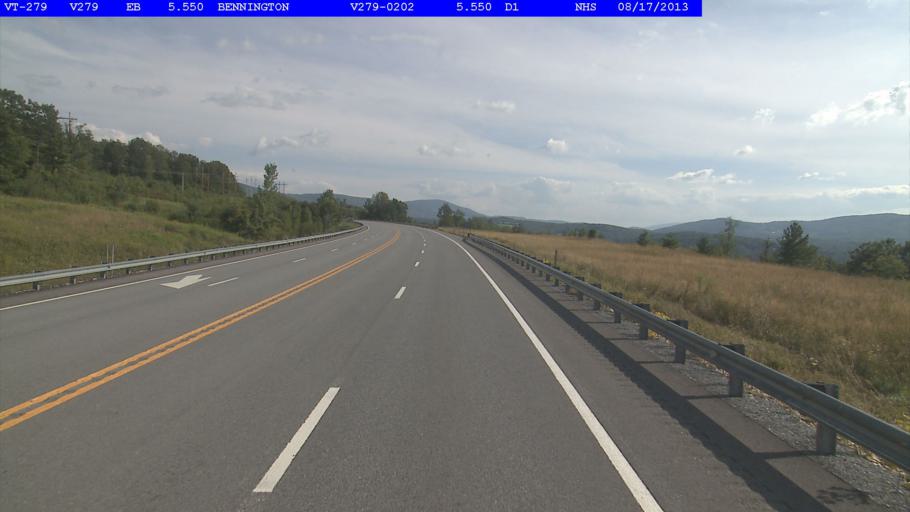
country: US
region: Vermont
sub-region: Bennington County
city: Bennington
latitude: 42.8938
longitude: -73.1768
